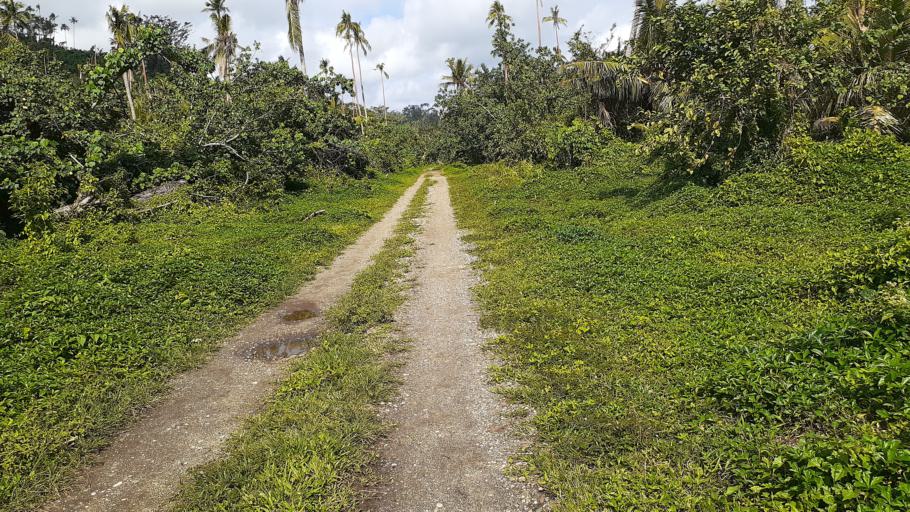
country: VU
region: Penama
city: Saratamata
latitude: -15.9341
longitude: 168.1910
